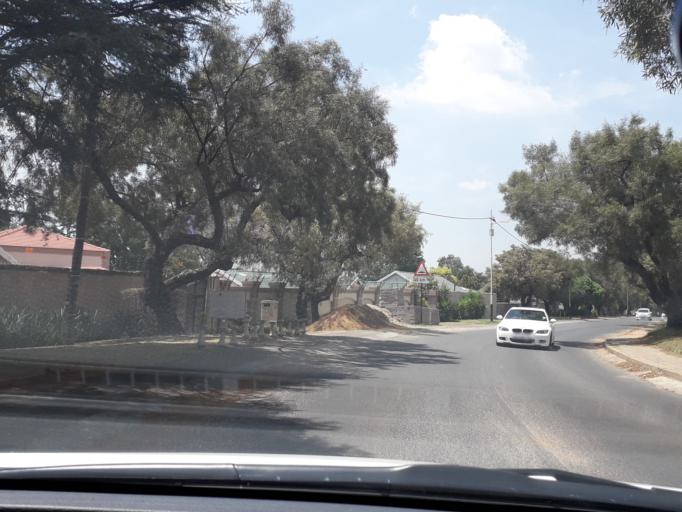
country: ZA
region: Gauteng
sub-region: City of Johannesburg Metropolitan Municipality
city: Johannesburg
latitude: -26.1078
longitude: 28.0043
